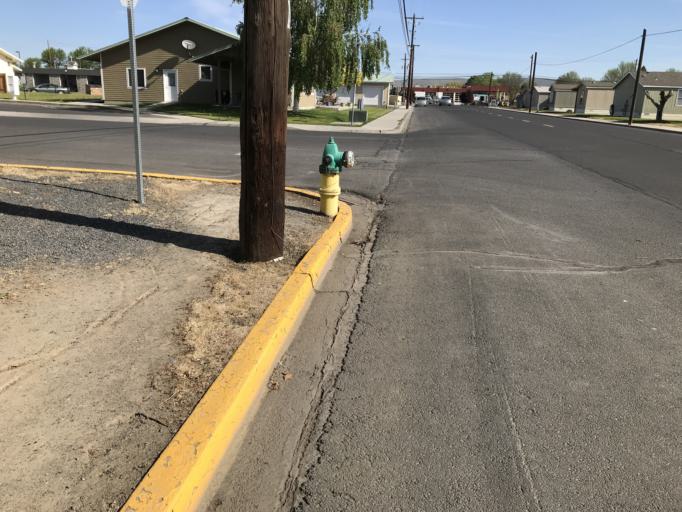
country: US
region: Washington
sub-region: Grant County
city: Quincy
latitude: 47.2320
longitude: -119.8589
